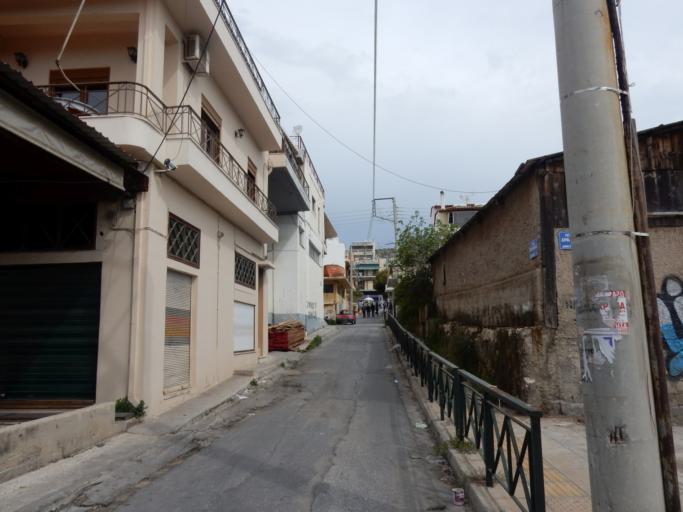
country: GR
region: Attica
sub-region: Nomos Piraios
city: Perama
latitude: 37.9633
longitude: 23.5680
